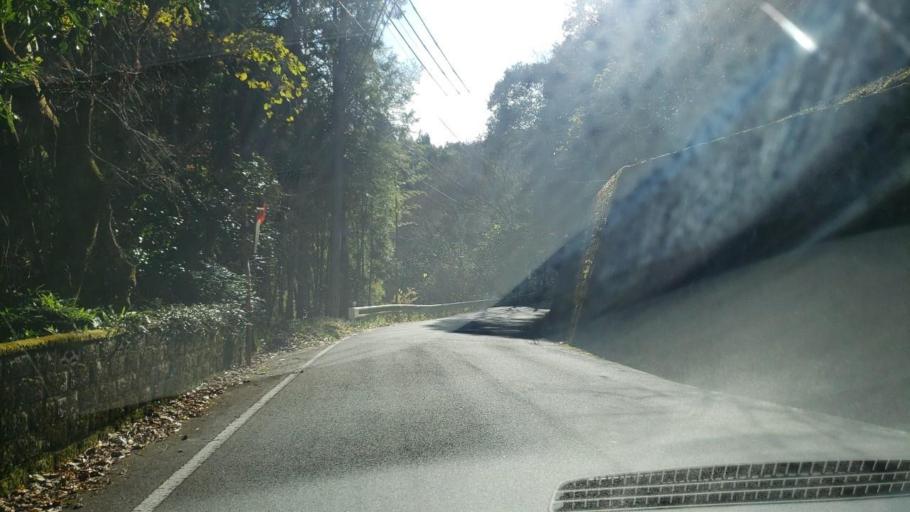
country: JP
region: Tokushima
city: Wakimachi
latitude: 34.0157
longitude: 134.0332
